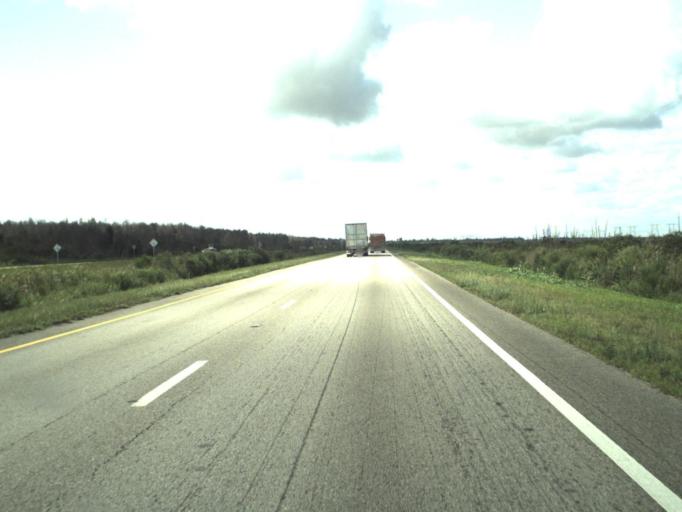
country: US
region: Florida
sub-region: Miami-Dade County
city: Palm Springs North
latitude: 25.9813
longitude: -80.4321
